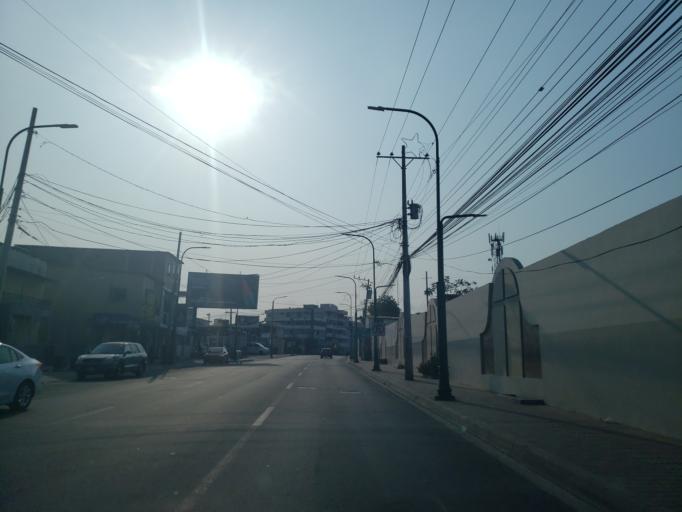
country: EC
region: Manabi
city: Manta
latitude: -0.9450
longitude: -80.7360
